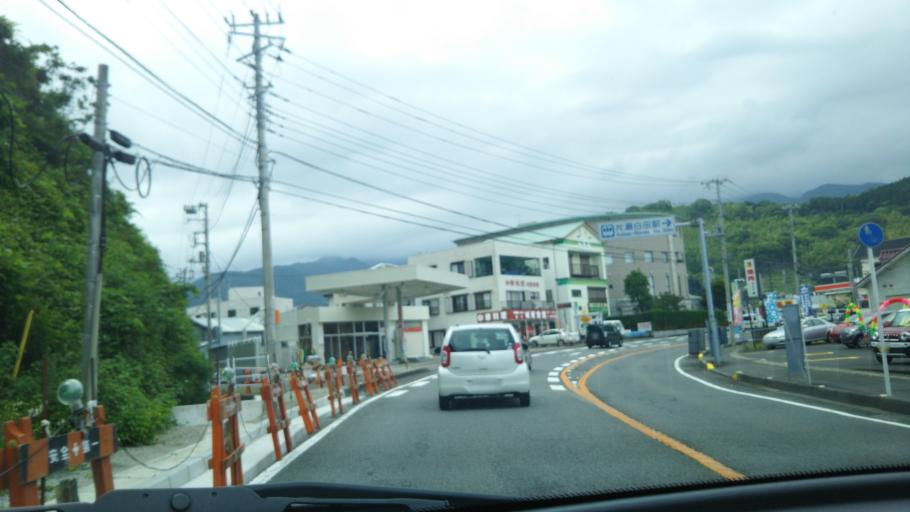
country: JP
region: Shizuoka
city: Ito
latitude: 34.8030
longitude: 139.0588
